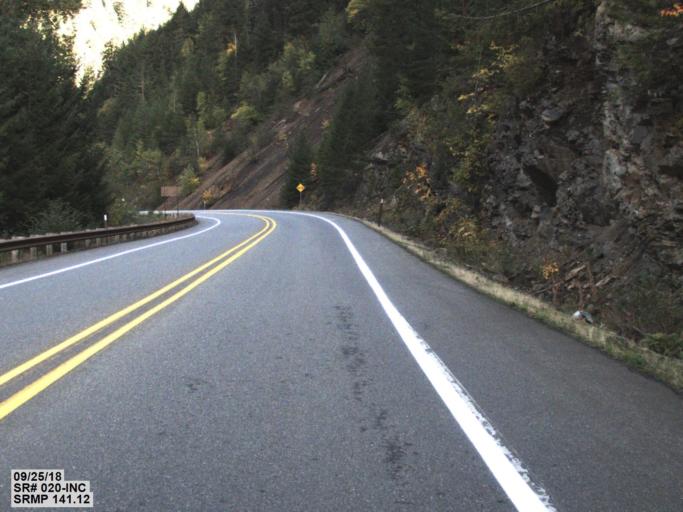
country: US
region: Washington
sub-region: Snohomish County
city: Darrington
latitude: 48.7061
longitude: -120.9214
